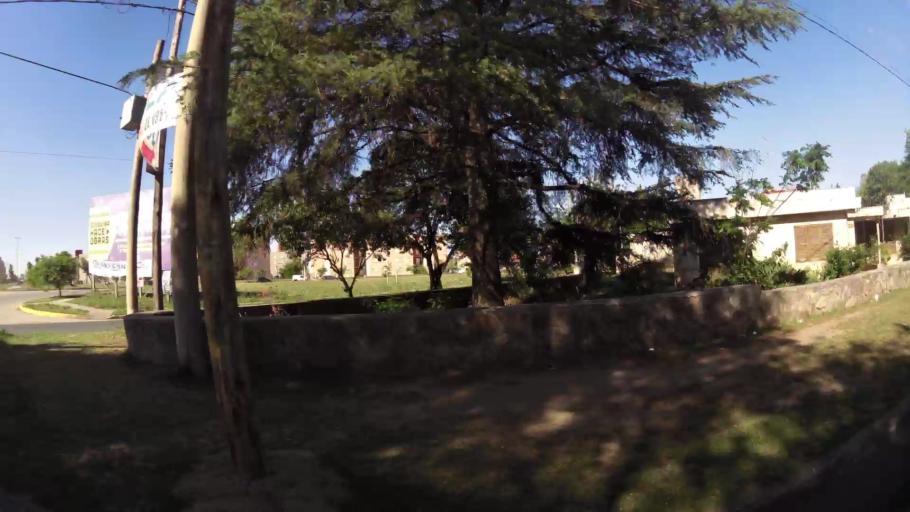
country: AR
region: Cordoba
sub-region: Departamento de Capital
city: Cordoba
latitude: -31.3575
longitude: -64.1916
